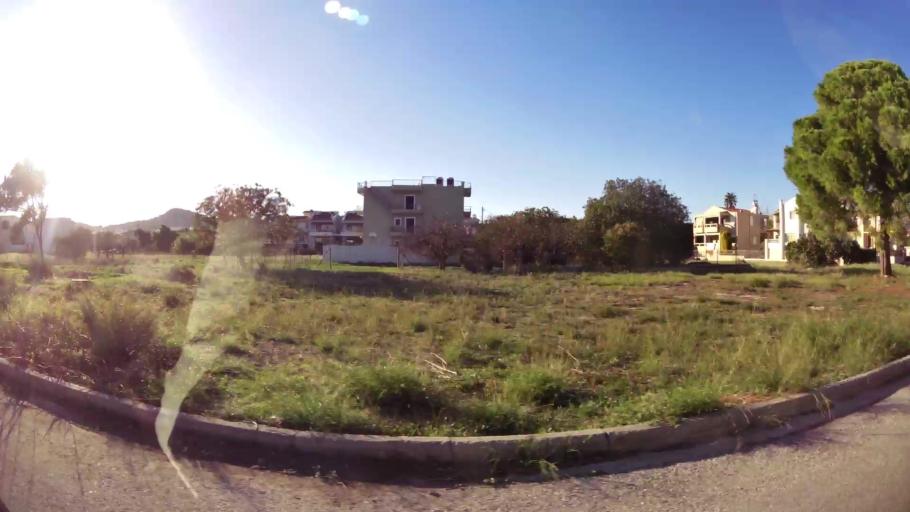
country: GR
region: Attica
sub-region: Nomarchia Anatolikis Attikis
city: Vari
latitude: 37.8232
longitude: 23.8105
